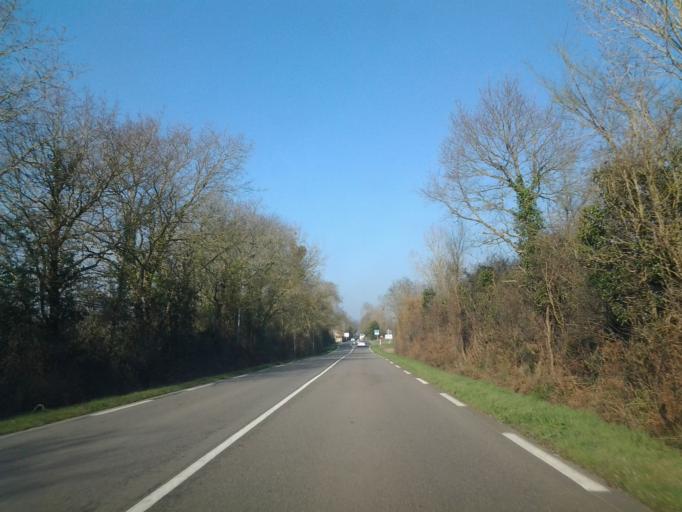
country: FR
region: Pays de la Loire
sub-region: Departement de la Vendee
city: Saint-Christophe-du-Ligneron
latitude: 46.8148
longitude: -1.7538
